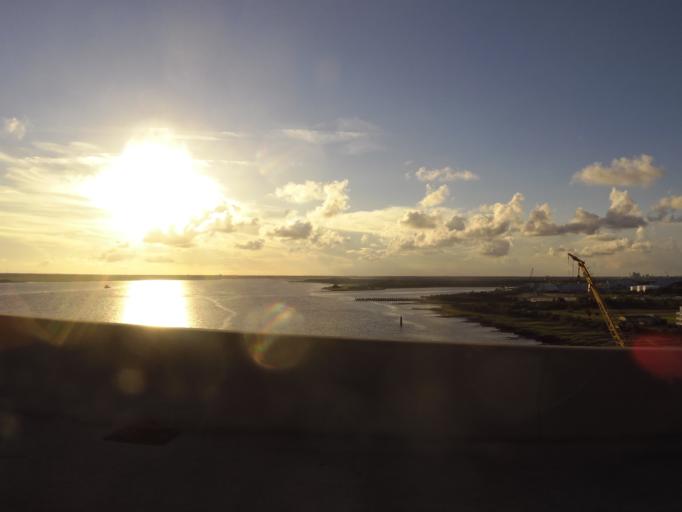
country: US
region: Georgia
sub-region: Glynn County
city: Brunswick
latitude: 31.1215
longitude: -81.4827
